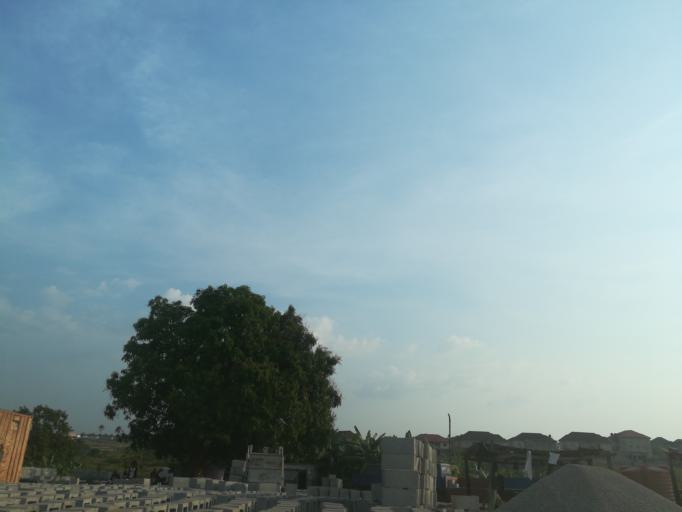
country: NG
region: Abuja Federal Capital Territory
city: Abuja
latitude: 9.1026
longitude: 7.3726
